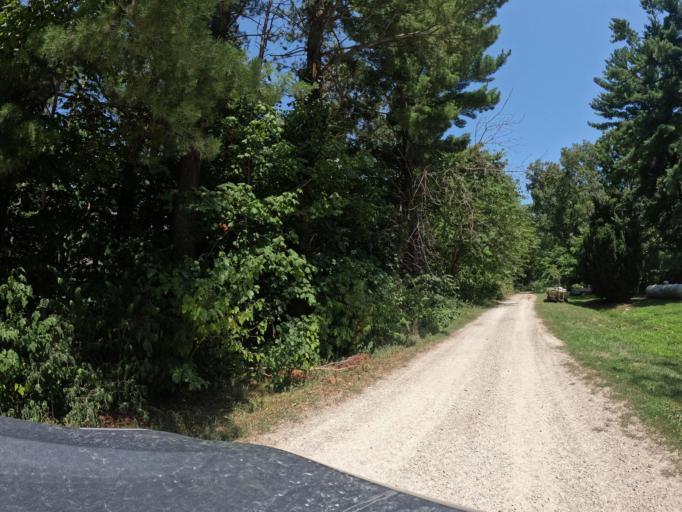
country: US
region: Iowa
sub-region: Henry County
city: Mount Pleasant
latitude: 40.9732
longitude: -91.6598
